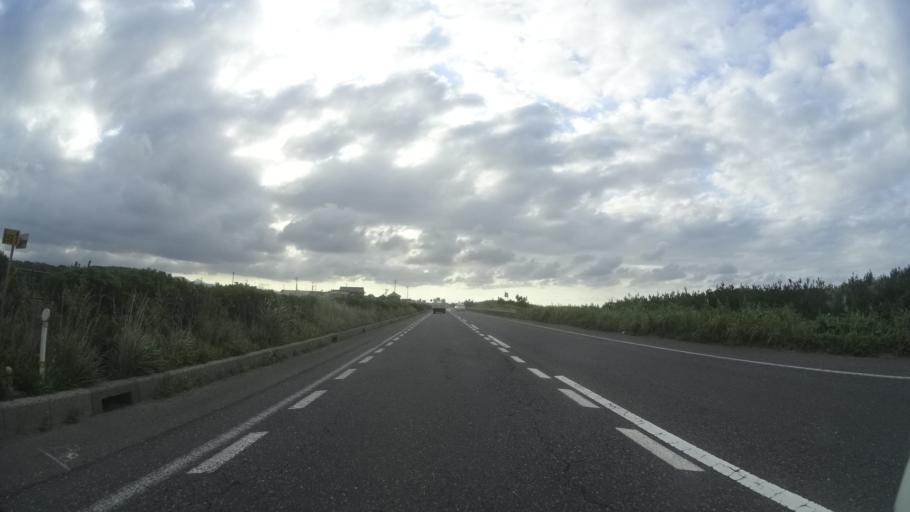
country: JP
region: Tottori
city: Kurayoshi
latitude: 35.5012
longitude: 133.7341
